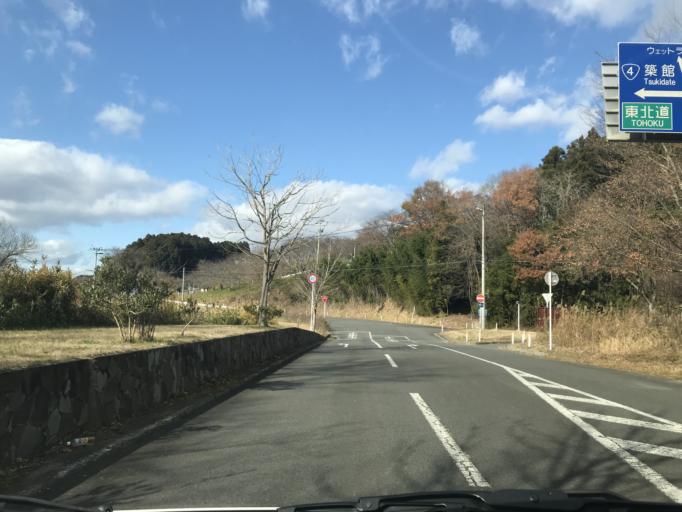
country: JP
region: Miyagi
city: Kogota
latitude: 38.7241
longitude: 141.0862
